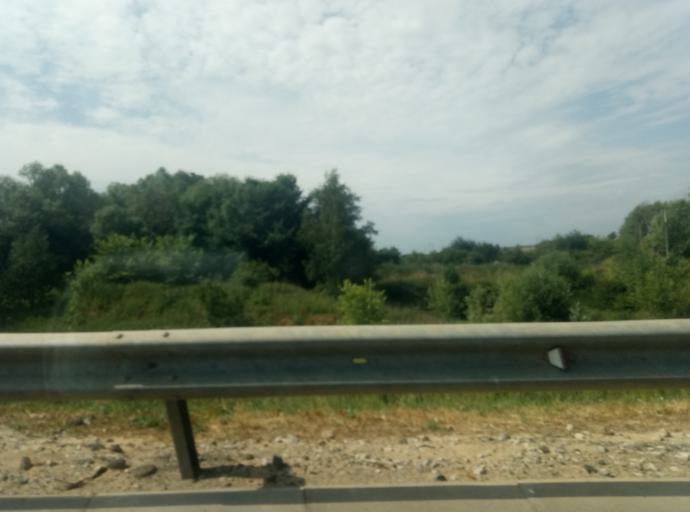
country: RU
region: Tula
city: Dubovka
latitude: 53.8677
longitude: 38.0670
